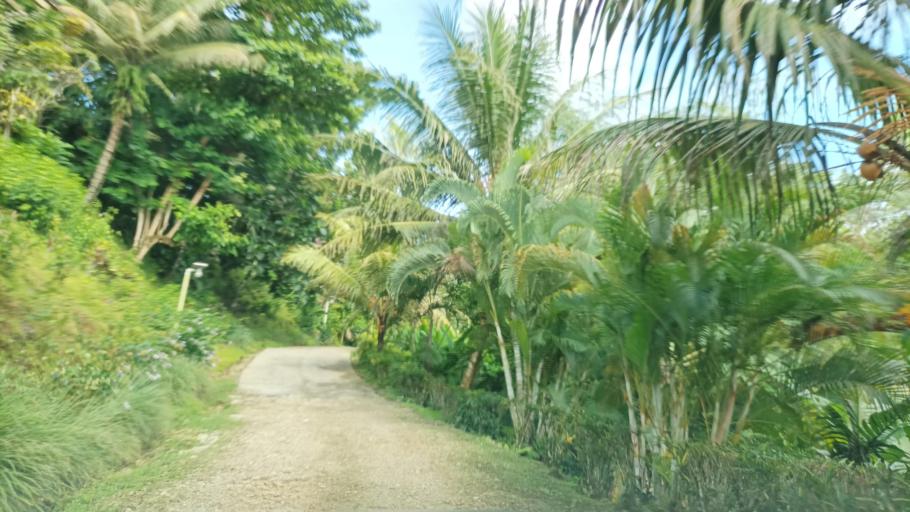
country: FM
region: Pohnpei
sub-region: Kolonia Municipality
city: Kolonia Town
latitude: 6.9606
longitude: 158.2053
